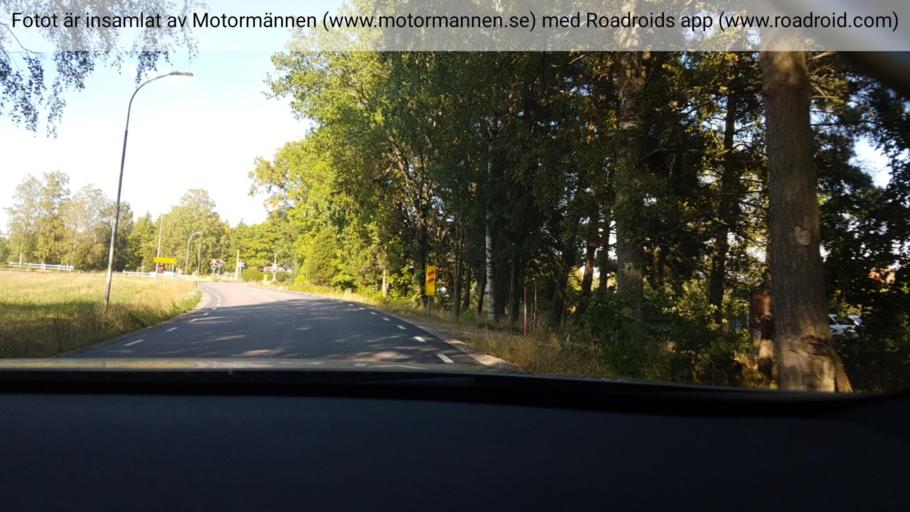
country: SE
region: Vaestra Goetaland
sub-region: Gotene Kommun
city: Goetene
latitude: 58.6237
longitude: 13.6214
